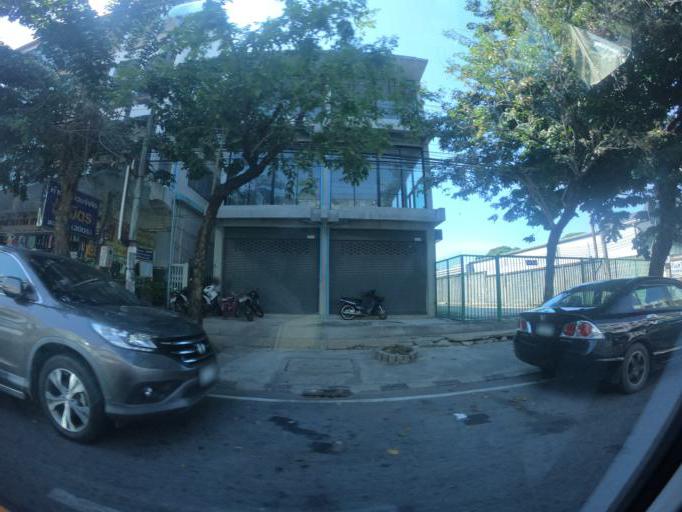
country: TH
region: Khon Kaen
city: Khon Kaen
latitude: 16.3807
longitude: 102.9331
